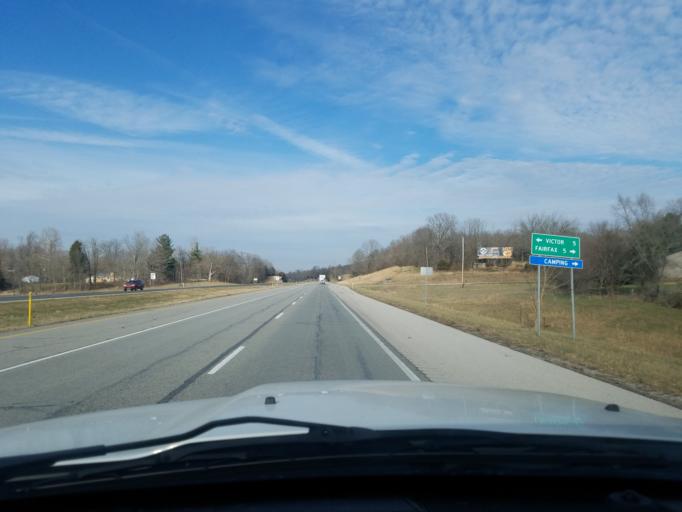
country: US
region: Indiana
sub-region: Monroe County
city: Bloomington
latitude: 39.0696
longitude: -86.5359
